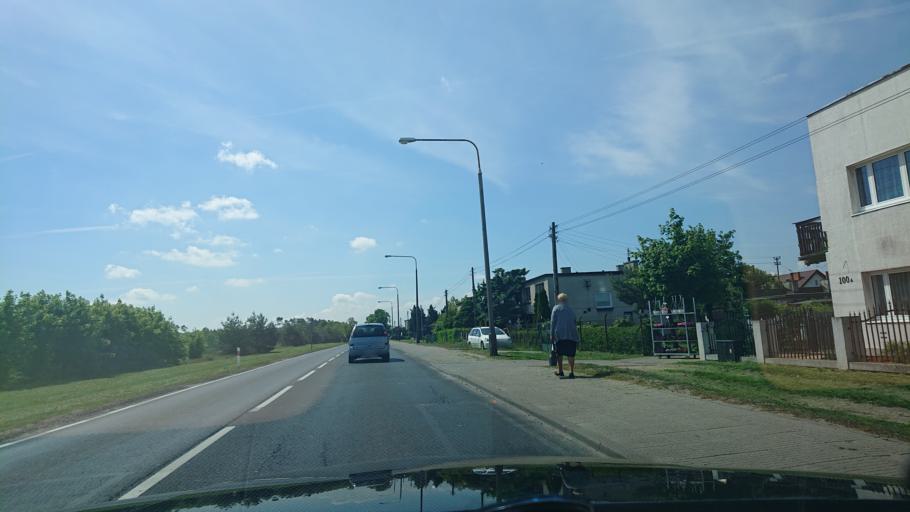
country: PL
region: Greater Poland Voivodeship
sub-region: Powiat gnieznienski
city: Gniezno
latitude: 52.5102
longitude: 17.5950
